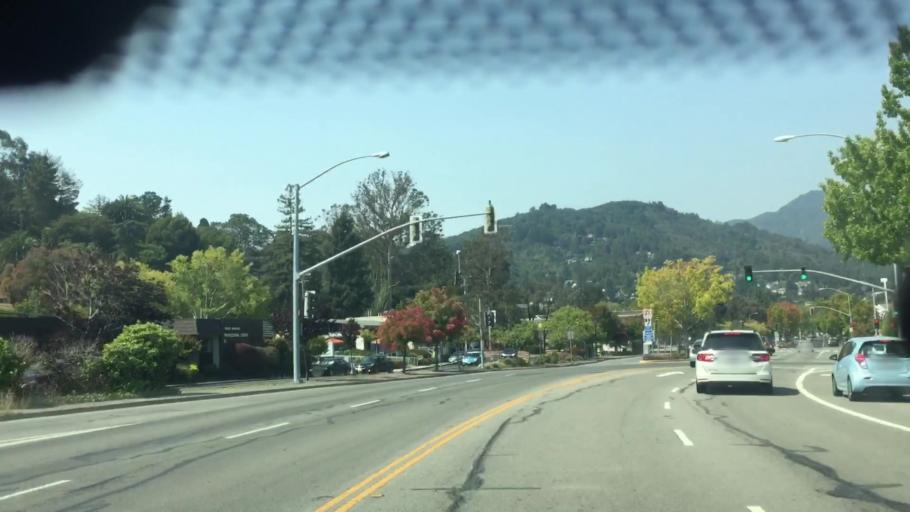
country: US
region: California
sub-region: Marin County
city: Corte Madera
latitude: 37.9251
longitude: -122.5170
